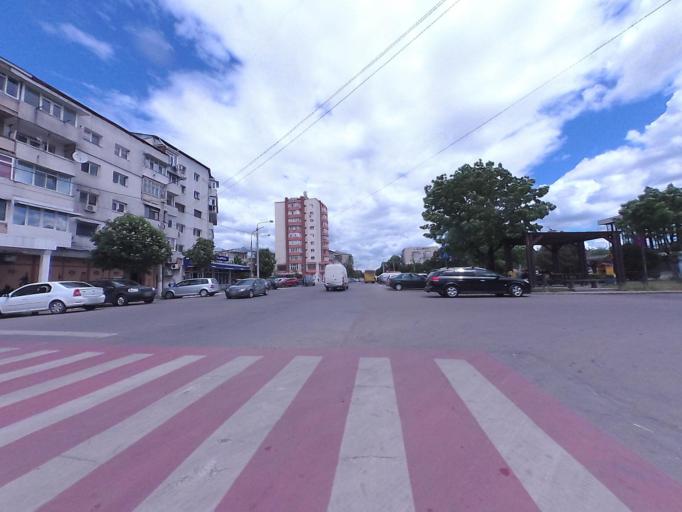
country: RO
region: Vaslui
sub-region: Municipiul Barlad
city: Barlad
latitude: 46.2154
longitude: 27.6719
